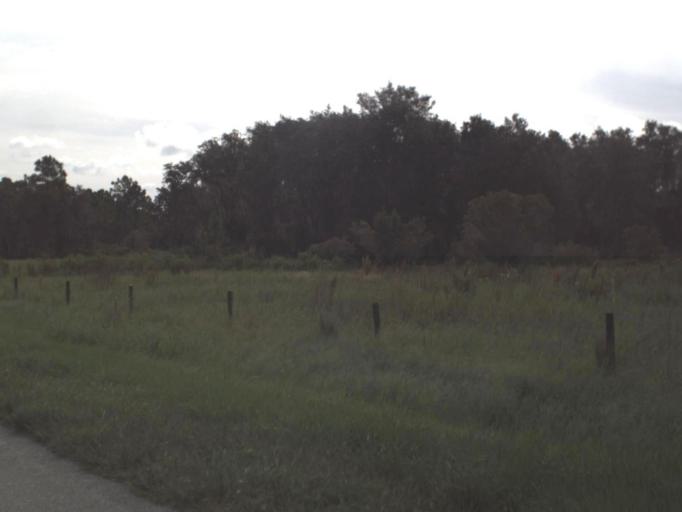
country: US
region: Florida
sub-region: Highlands County
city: Placid Lakes
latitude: 27.2088
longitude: -81.4864
